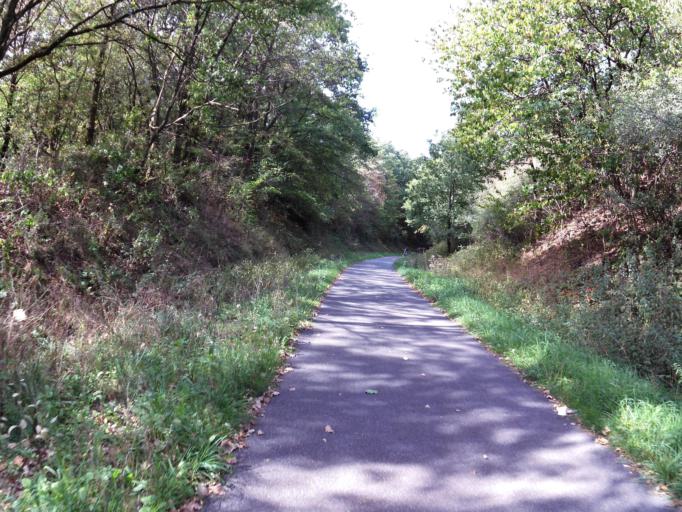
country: DE
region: Rheinland-Pfalz
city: Lichtenborn
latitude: 50.1145
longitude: 6.2697
